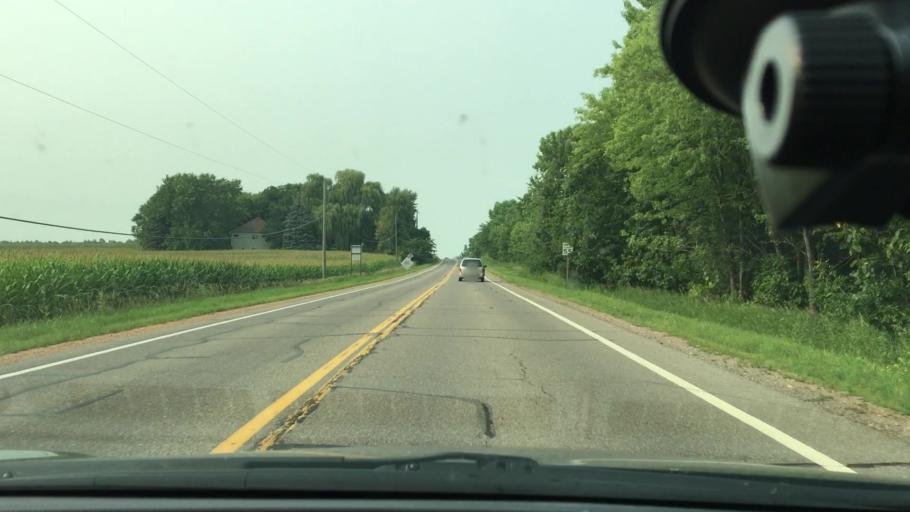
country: US
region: Minnesota
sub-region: Hennepin County
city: Osseo
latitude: 45.1435
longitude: -93.4621
